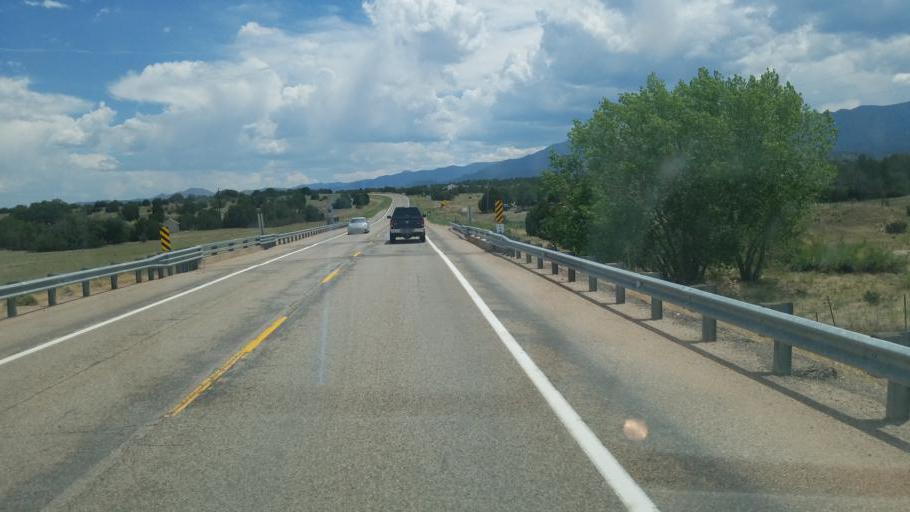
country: US
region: Colorado
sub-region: Fremont County
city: Florence
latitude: 38.3155
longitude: -105.1053
